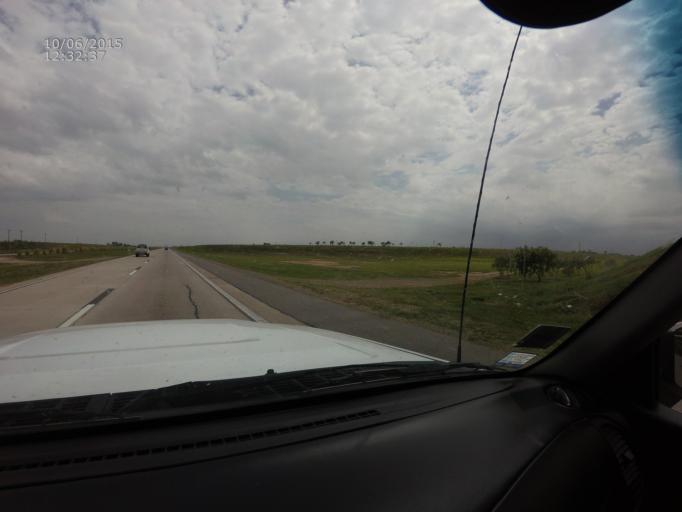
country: AR
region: Santa Fe
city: Carcarana
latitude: -32.8799
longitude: -61.1496
